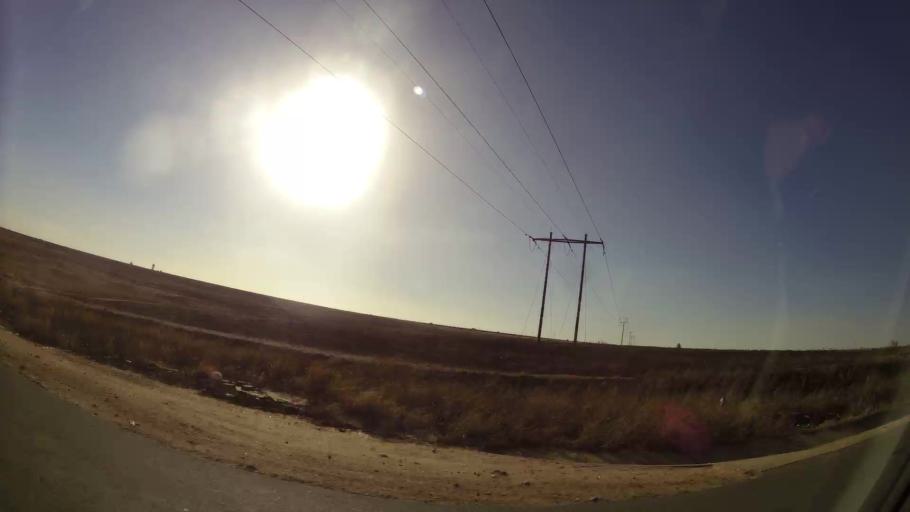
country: ZA
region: Gauteng
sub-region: City of Johannesburg Metropolitan Municipality
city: Diepsloot
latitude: -25.9453
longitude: 27.9727
